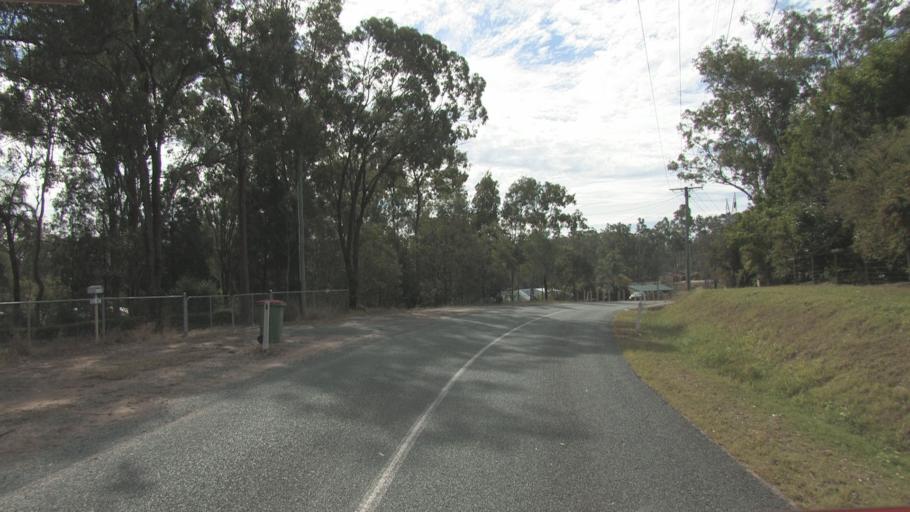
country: AU
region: Queensland
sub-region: Logan
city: North Maclean
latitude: -27.7425
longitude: 152.9735
